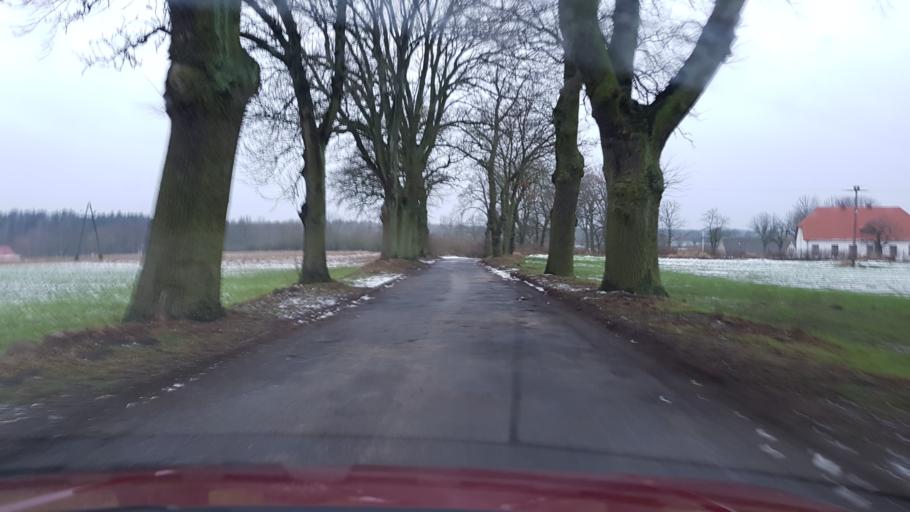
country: PL
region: West Pomeranian Voivodeship
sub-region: Powiat goleniowski
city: Mosty
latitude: 53.5037
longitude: 14.9139
